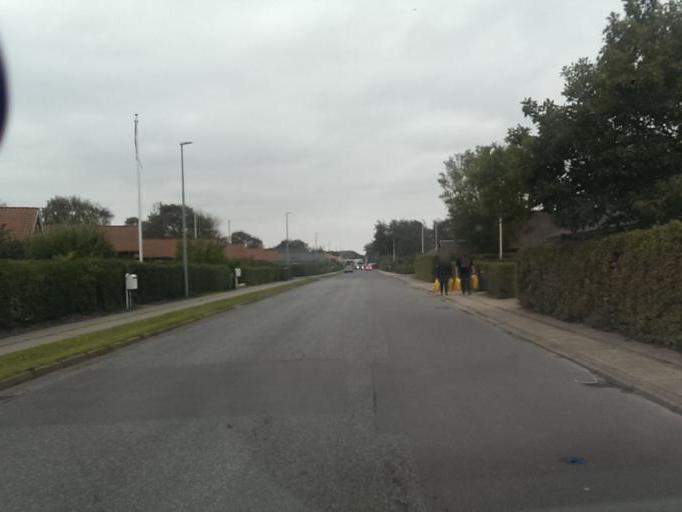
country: DK
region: South Denmark
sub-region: Esbjerg Kommune
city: Bramming
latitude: 55.4693
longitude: 8.6916
